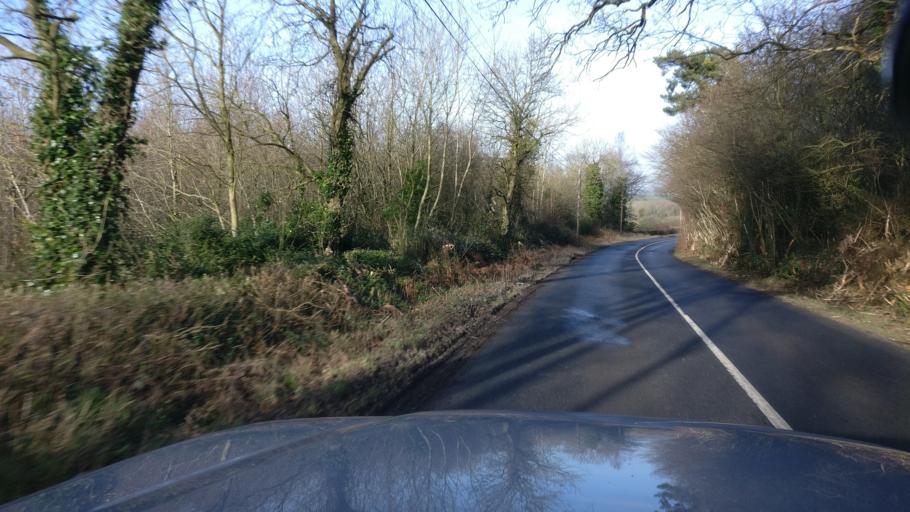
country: IE
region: Leinster
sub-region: Laois
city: Stradbally
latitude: 52.9464
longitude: -7.2004
